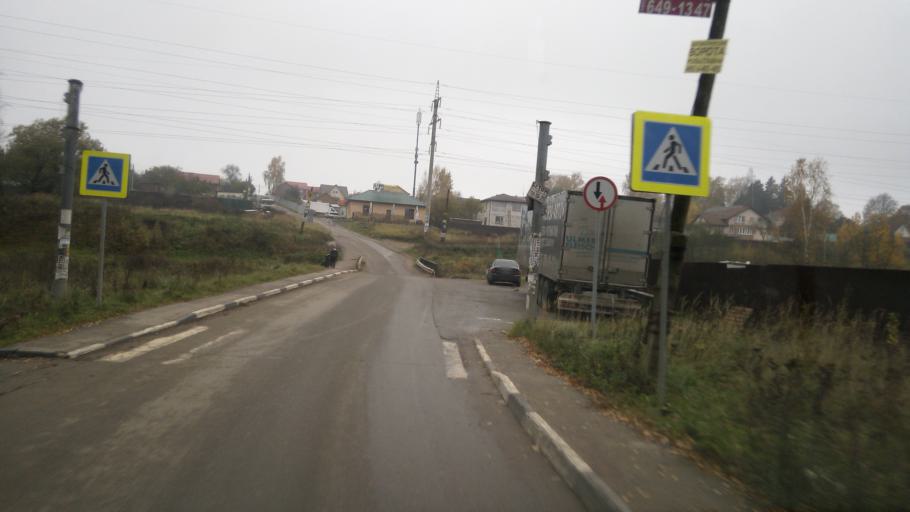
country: RU
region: Moskovskaya
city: Skhodnya
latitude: 55.9360
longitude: 37.2883
